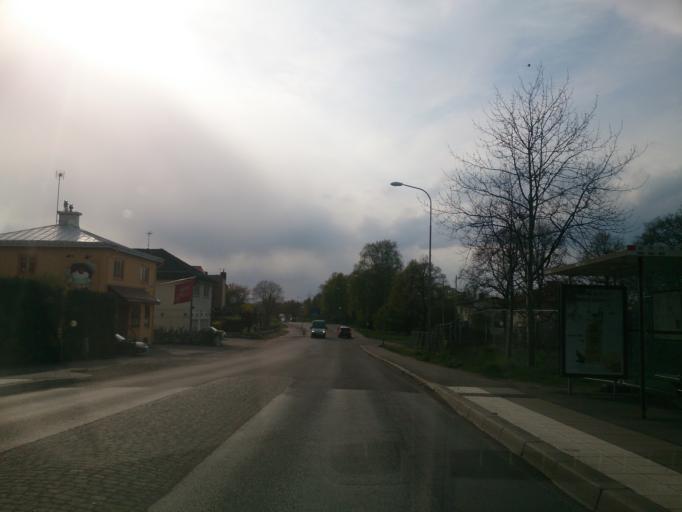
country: SE
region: OEstergoetland
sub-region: Norrkopings Kommun
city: Norrkoping
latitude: 58.5842
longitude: 16.1554
